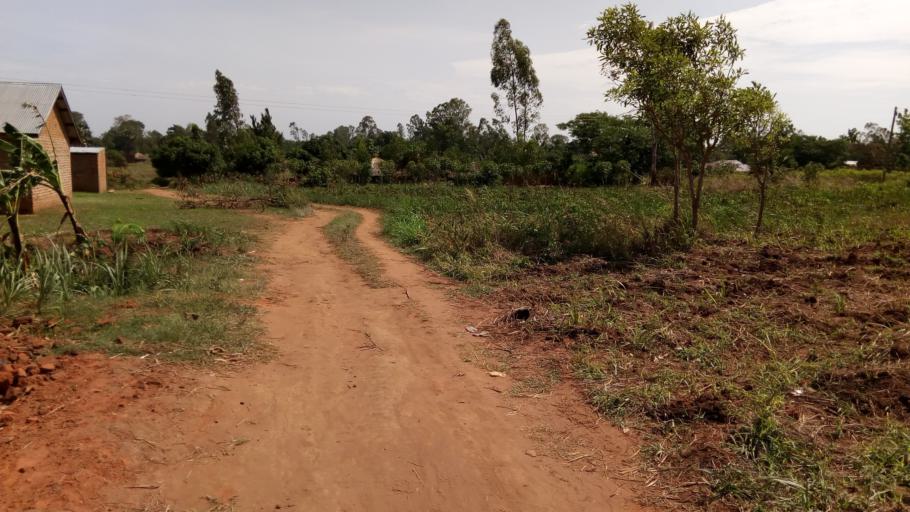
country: UG
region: Northern Region
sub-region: Gulu District
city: Gulu
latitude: 2.7958
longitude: 32.3191
